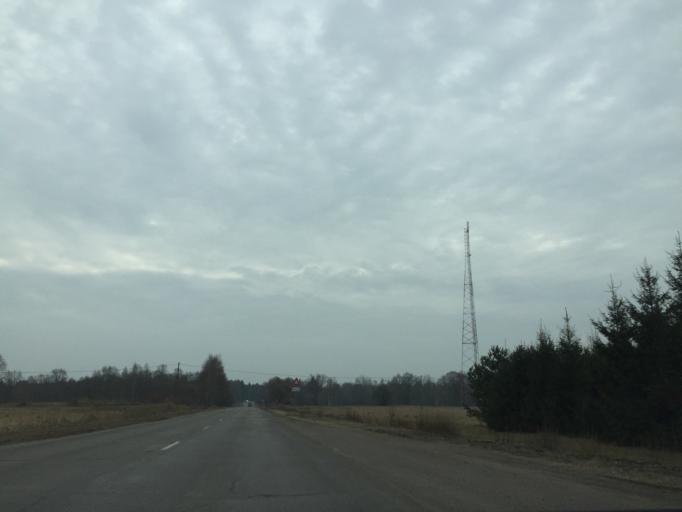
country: LV
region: Kekava
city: Balozi
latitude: 56.7722
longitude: 24.1110
